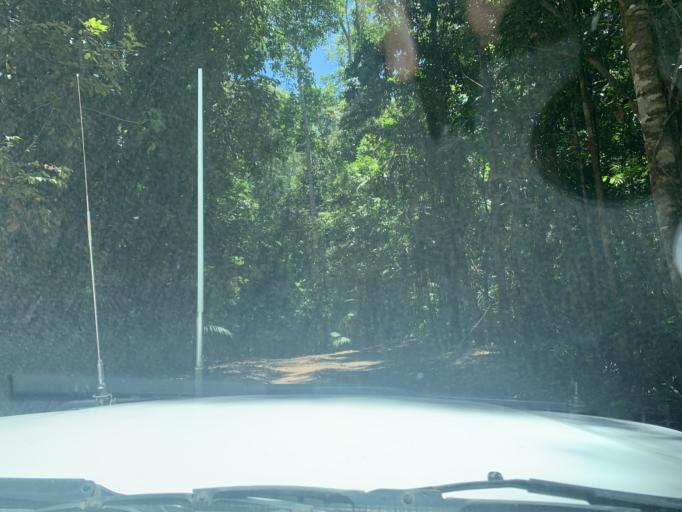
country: AU
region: Queensland
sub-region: Cairns
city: Redlynch
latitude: -16.9552
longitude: 145.6389
